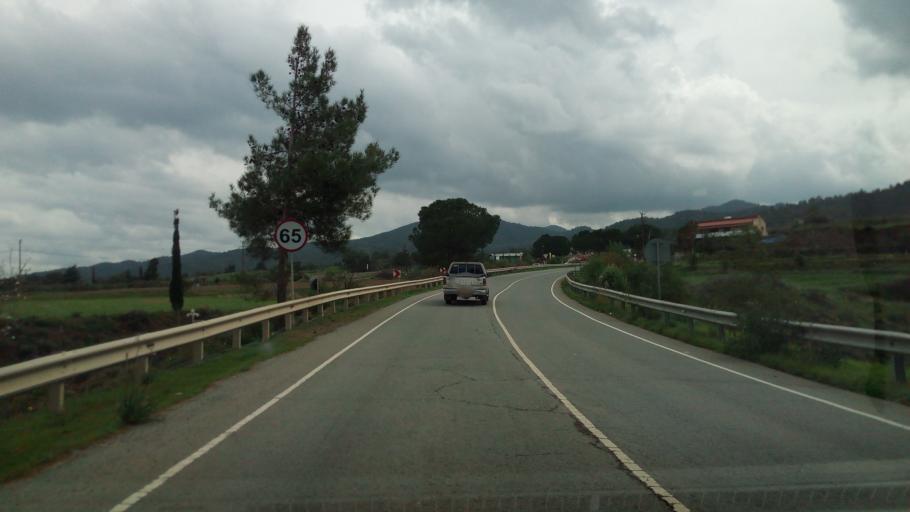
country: CY
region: Lefkosia
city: Lefka
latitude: 35.0718
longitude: 32.9243
